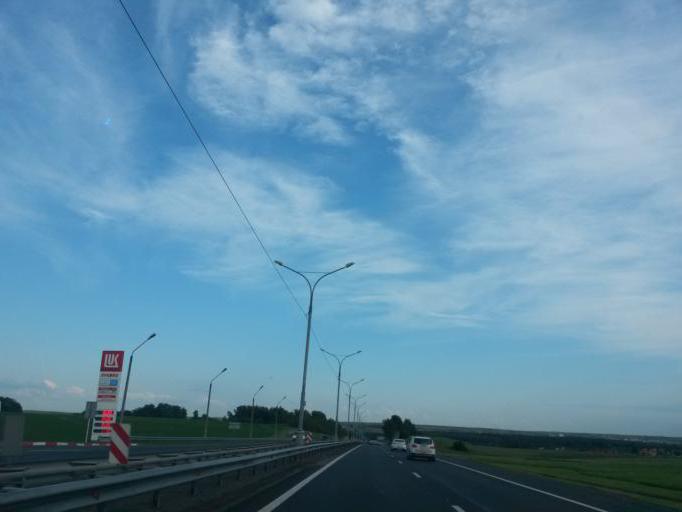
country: RU
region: Moskovskaya
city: Gorki-Leninskiye
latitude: 55.5089
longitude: 37.8331
